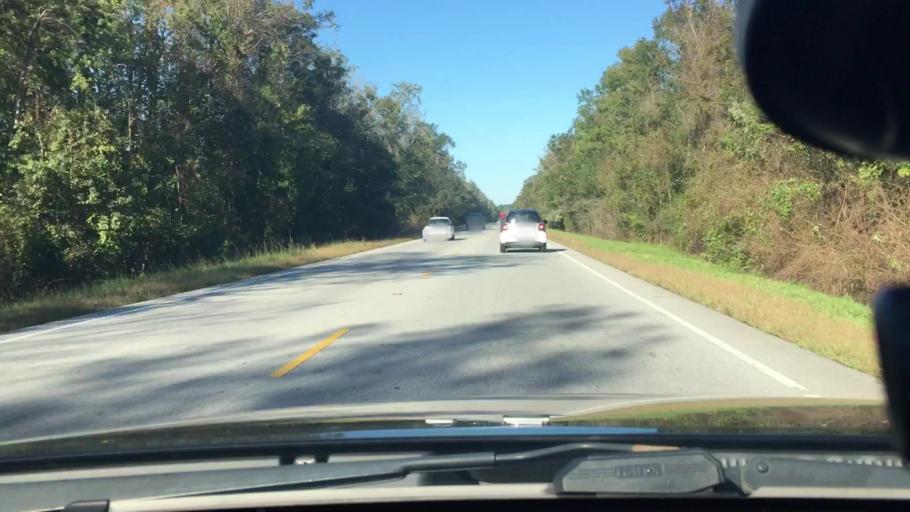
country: US
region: North Carolina
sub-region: Craven County
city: Vanceboro
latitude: 35.2017
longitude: -77.1290
